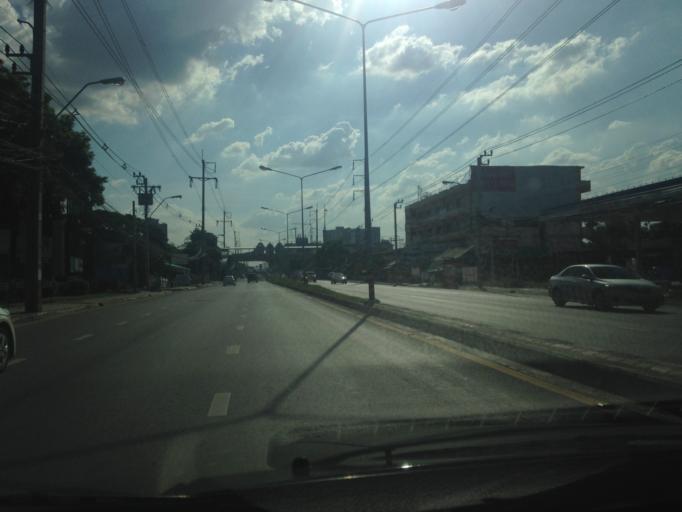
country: TH
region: Nonthaburi
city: Pak Kret
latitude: 13.9154
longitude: 100.5132
